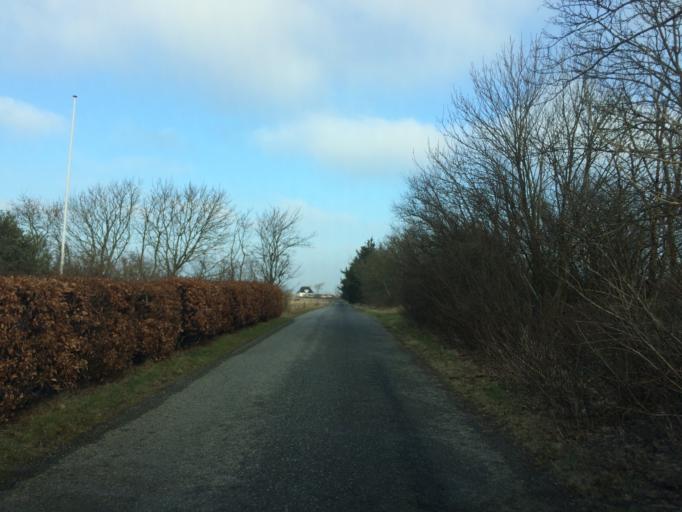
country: DK
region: South Denmark
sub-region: Varde Kommune
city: Oksbol
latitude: 55.5797
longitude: 8.3276
